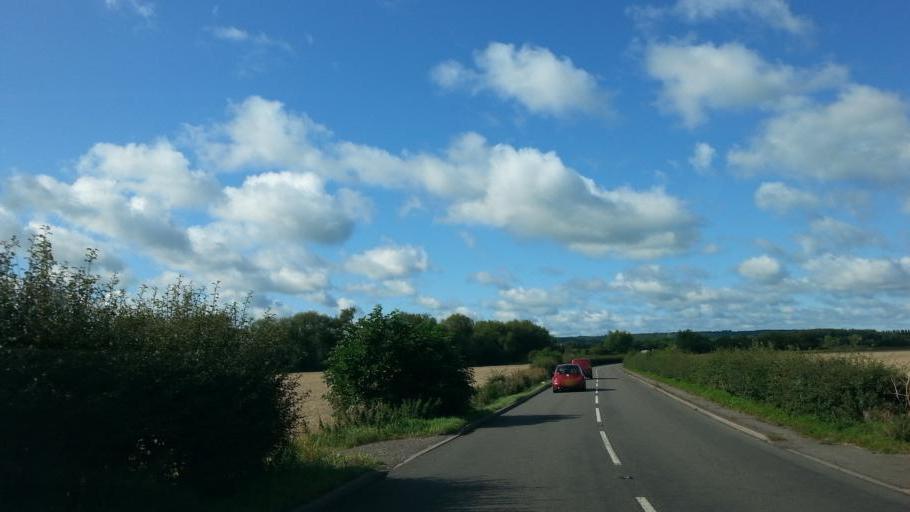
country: GB
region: England
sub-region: Derbyshire
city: Rodsley
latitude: 52.8798
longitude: -1.7547
